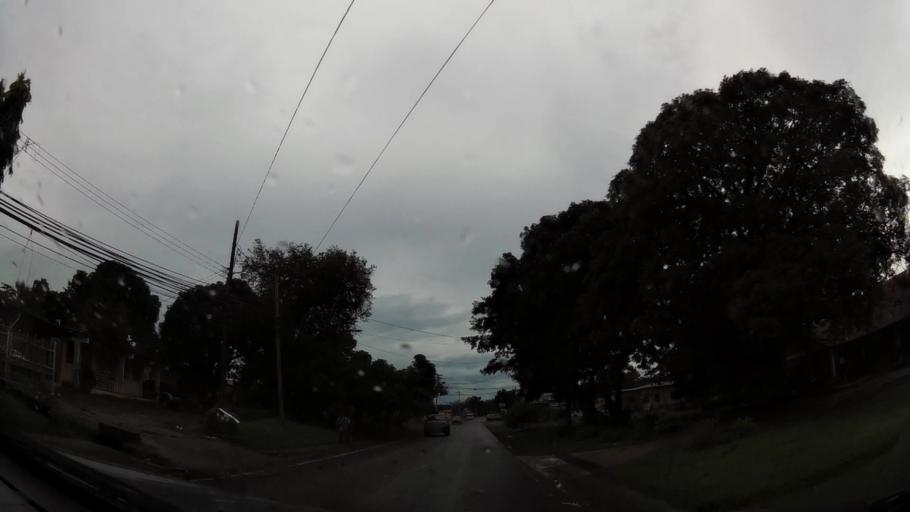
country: PA
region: Veraguas
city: Santiago de Veraguas
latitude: 8.0892
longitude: -80.9870
